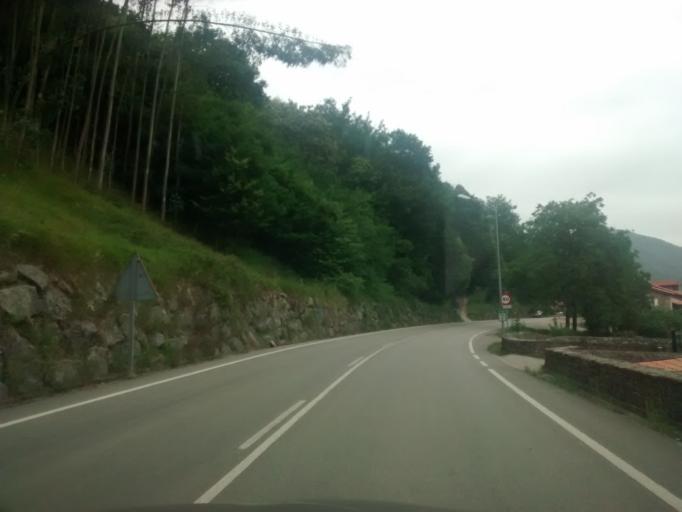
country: ES
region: Cantabria
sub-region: Provincia de Cantabria
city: Ruente
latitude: 43.2183
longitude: -4.3038
